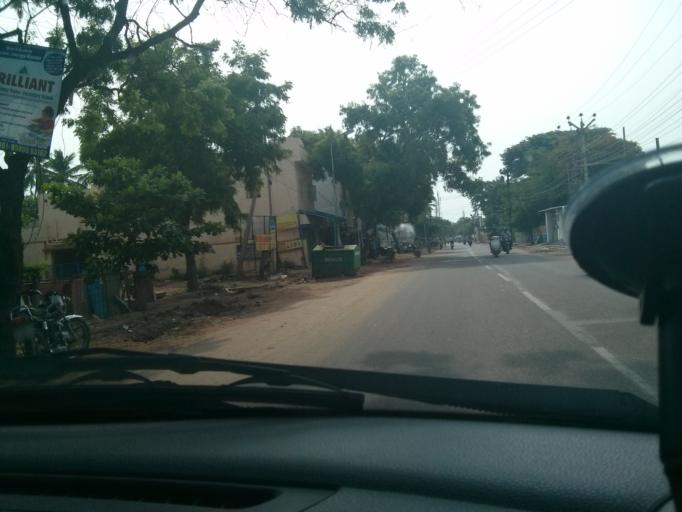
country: IN
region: Tamil Nadu
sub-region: Coimbatore
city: Coimbatore
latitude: 11.0343
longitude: 76.9620
